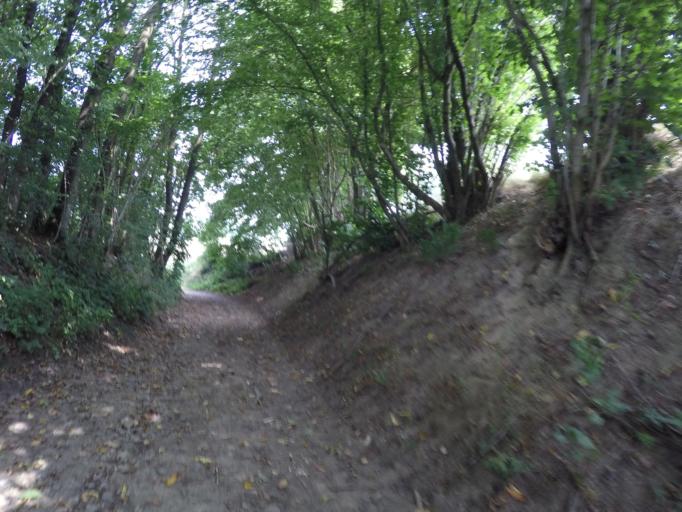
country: BE
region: Wallonia
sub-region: Province de Namur
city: Assesse
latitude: 50.3405
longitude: 4.9906
